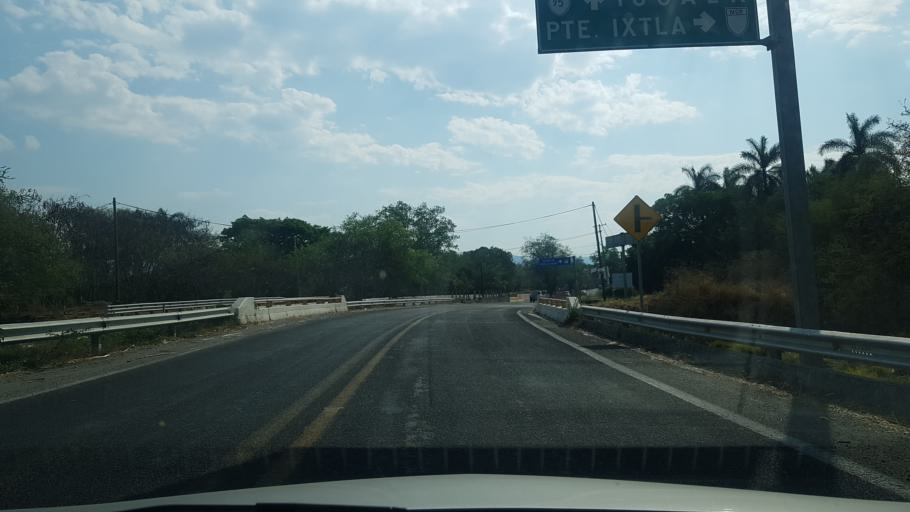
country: MX
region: Morelos
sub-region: Amacuzac
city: San Gabriel las Palmas
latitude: 18.6139
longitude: -99.3413
